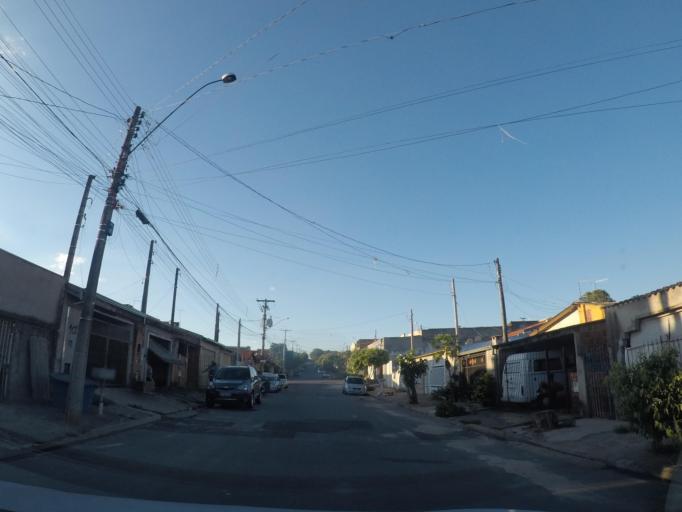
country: BR
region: Sao Paulo
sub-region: Sumare
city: Sumare
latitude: -22.8326
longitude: -47.2443
